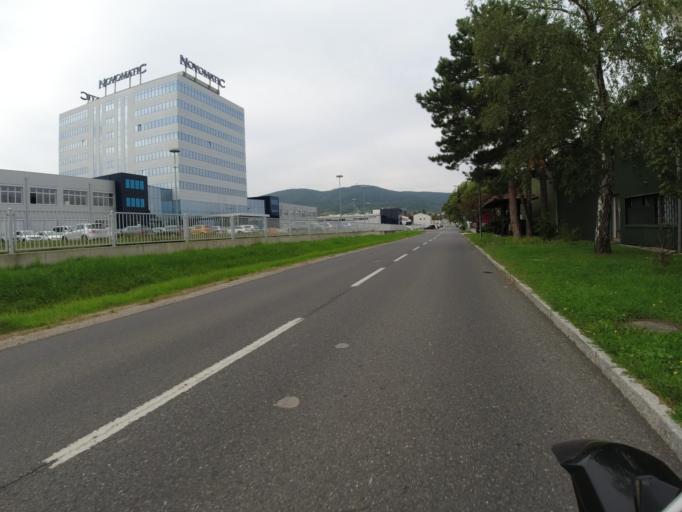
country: AT
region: Lower Austria
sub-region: Politischer Bezirk Modling
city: Gumpoldskirchen
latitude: 48.0359
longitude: 16.2949
